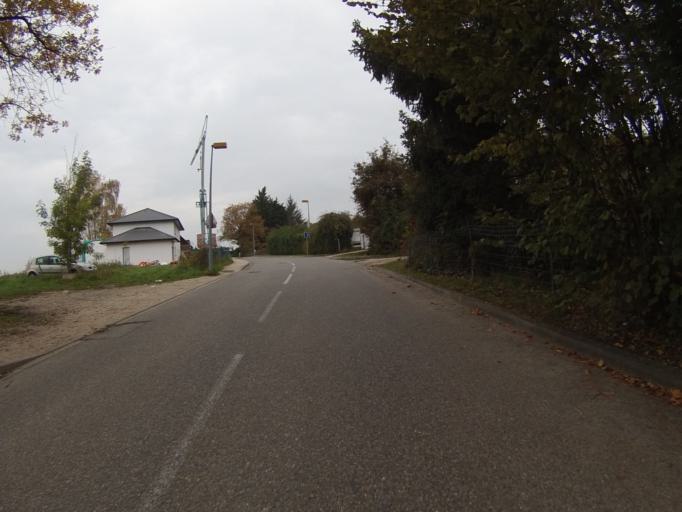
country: CH
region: Geneva
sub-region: Geneva
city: Meyrin
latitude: 46.2535
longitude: 6.0860
